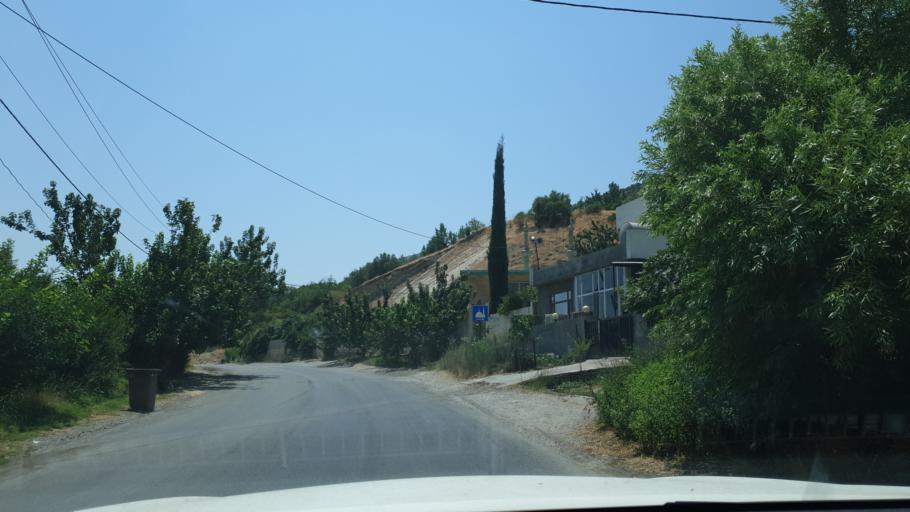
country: IQ
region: Arbil
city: Nahiyat Hiran
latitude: 36.2870
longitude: 44.4857
